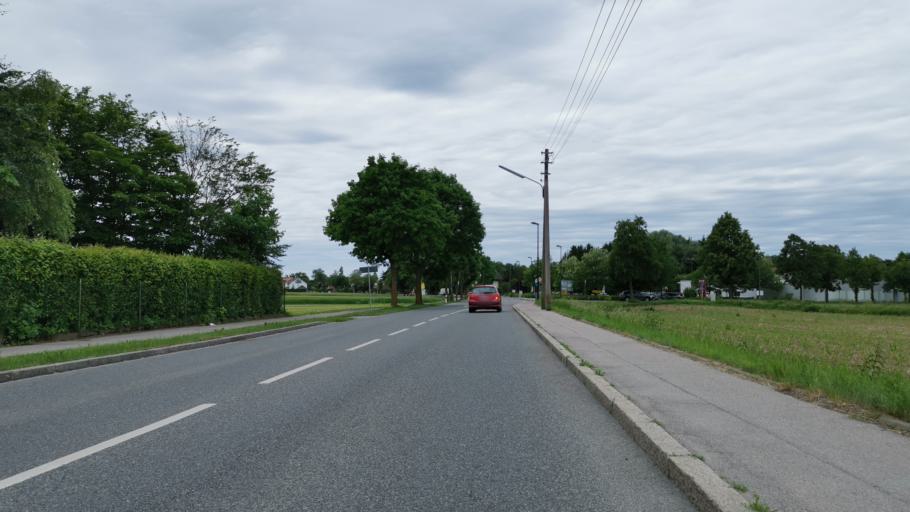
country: DE
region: Bavaria
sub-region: Upper Bavaria
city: Emmering
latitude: 48.1810
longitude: 11.2938
